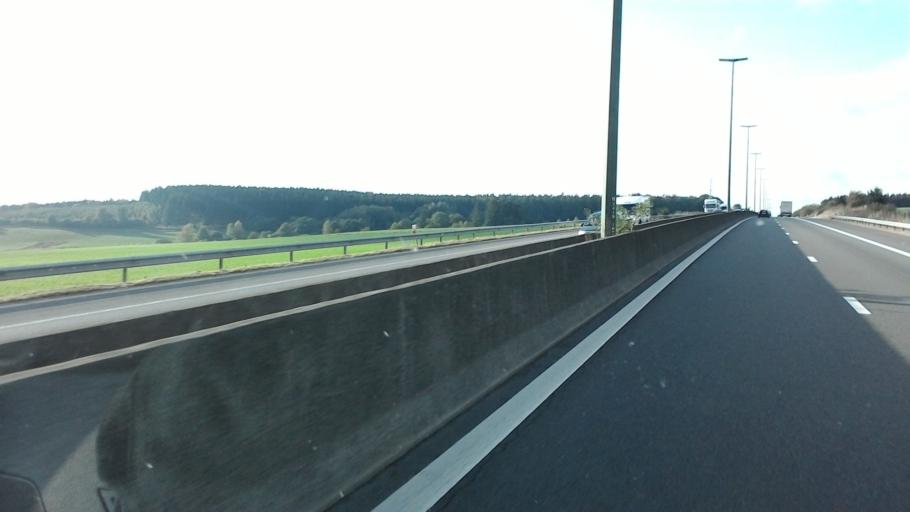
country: BE
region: Wallonia
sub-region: Province du Luxembourg
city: Leglise
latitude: 49.7791
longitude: 5.5407
